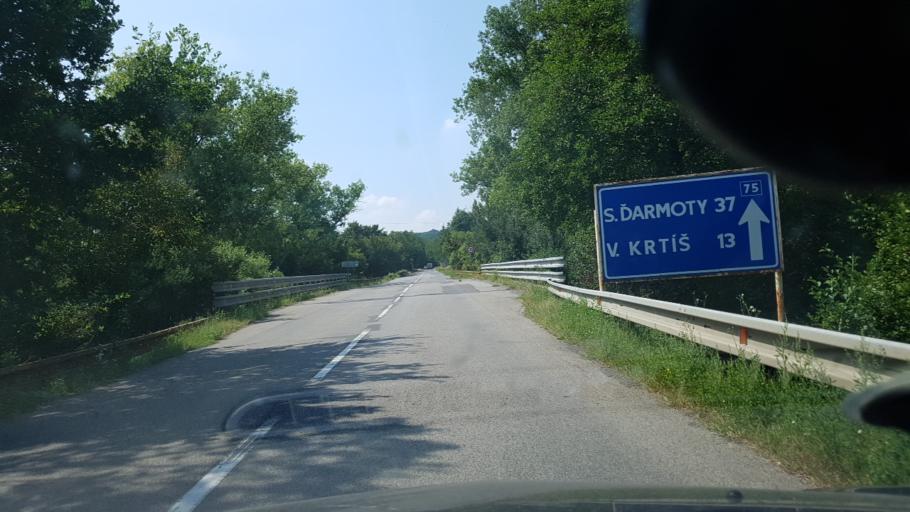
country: SK
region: Banskobystricky
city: Velky Krtis
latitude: 48.2680
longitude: 19.4479
